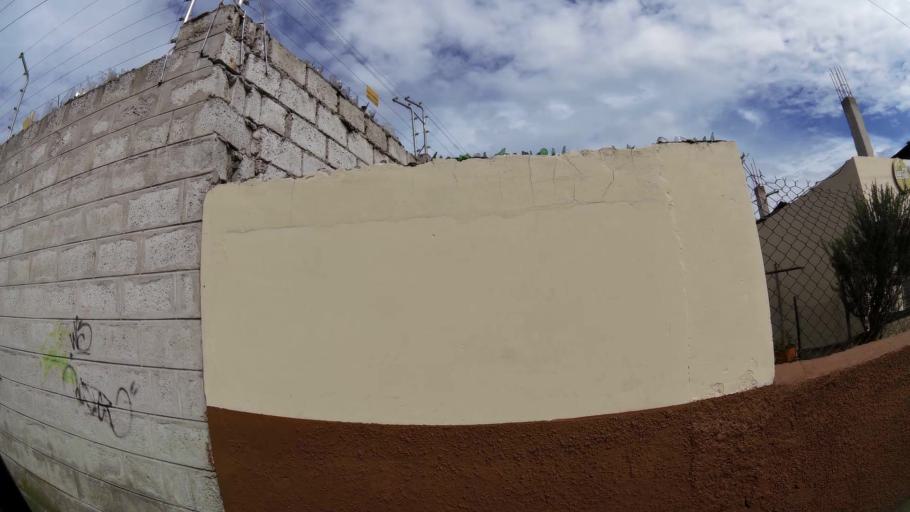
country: EC
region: Tungurahua
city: Ambato
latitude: -1.2490
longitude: -78.6184
